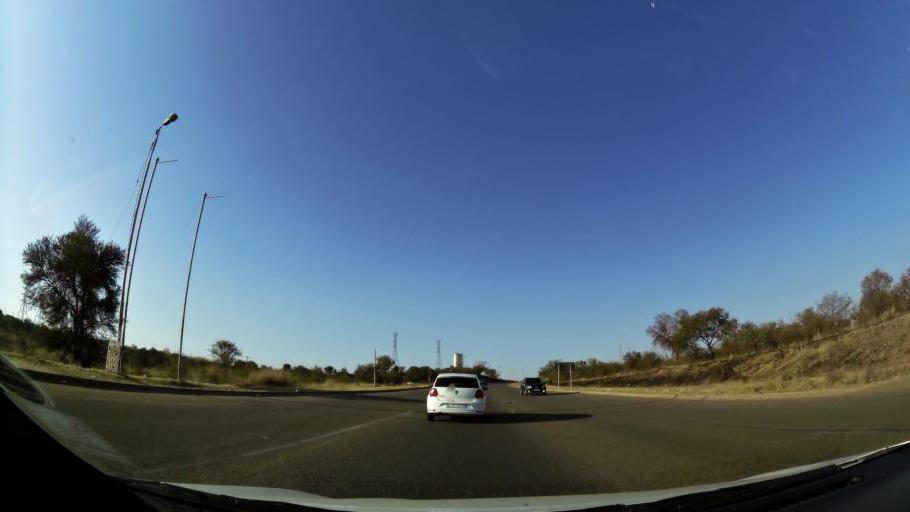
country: ZA
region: Gauteng
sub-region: City of Tshwane Metropolitan Municipality
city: Cullinan
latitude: -25.7420
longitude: 28.3767
